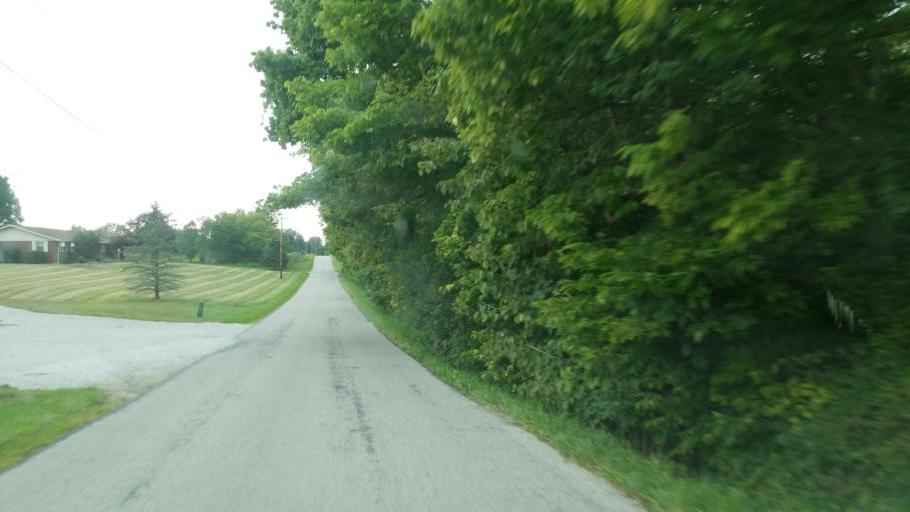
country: US
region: Ohio
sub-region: Crawford County
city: Galion
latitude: 40.7283
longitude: -82.8490
